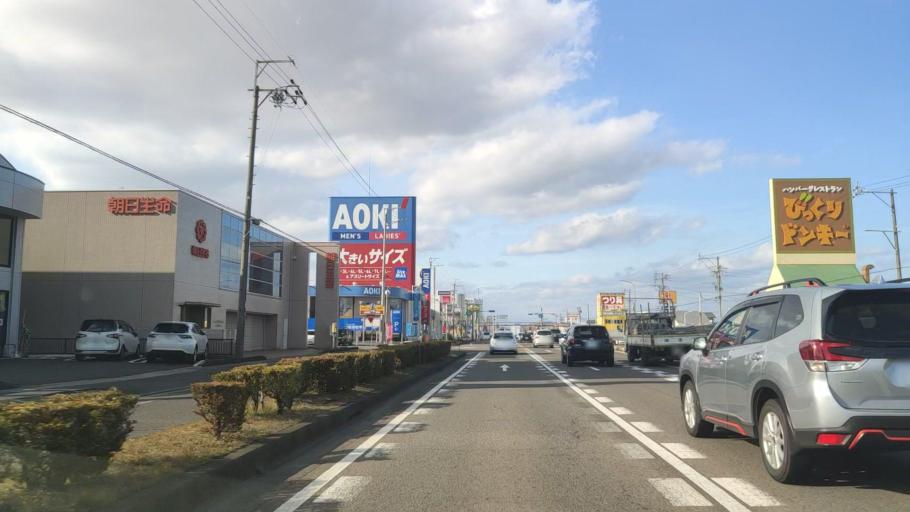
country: JP
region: Aichi
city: Ichinomiya
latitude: 35.3024
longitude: 136.8218
